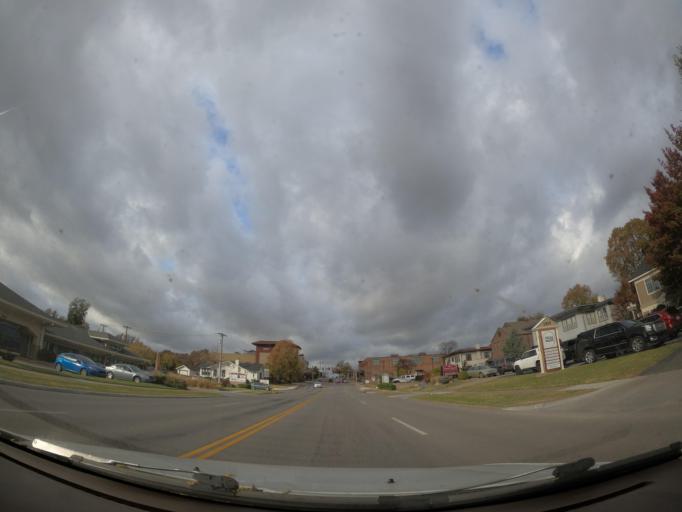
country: US
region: Oklahoma
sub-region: Tulsa County
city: Tulsa
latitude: 36.1406
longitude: -95.9652
